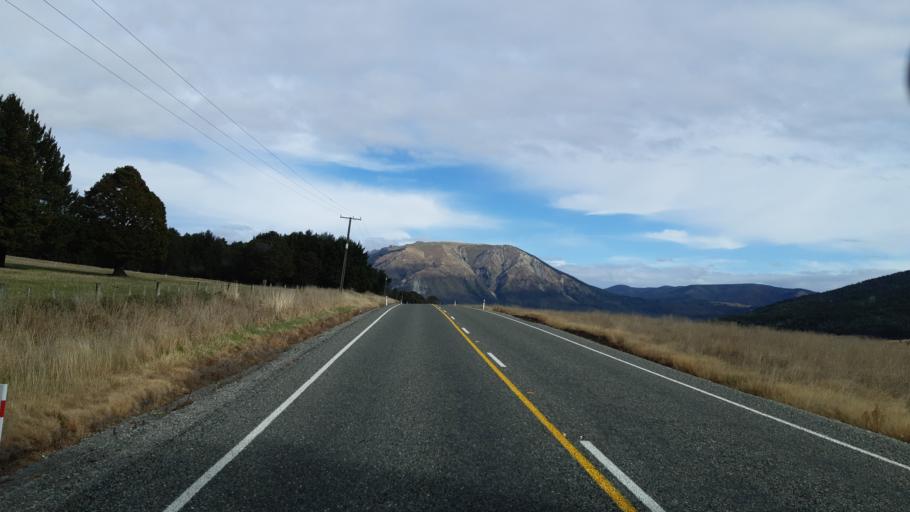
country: NZ
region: Tasman
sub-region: Tasman District
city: Wakefield
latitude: -41.7910
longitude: 172.8814
